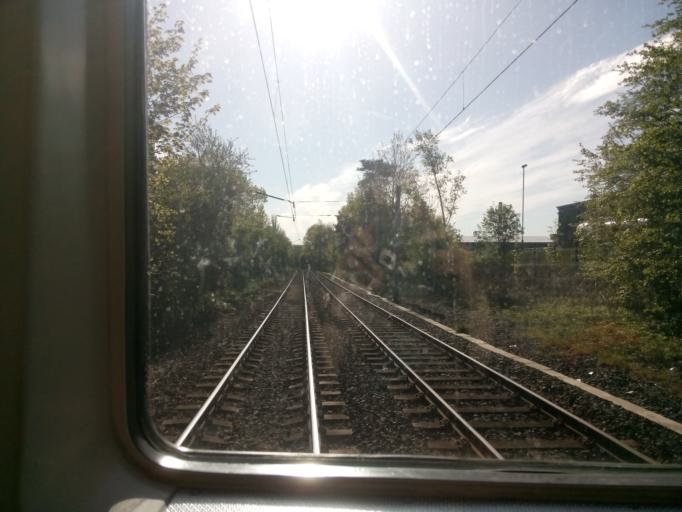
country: GB
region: England
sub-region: Newcastle upon Tyne
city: Hazlerigg
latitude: 55.0138
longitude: -1.6569
